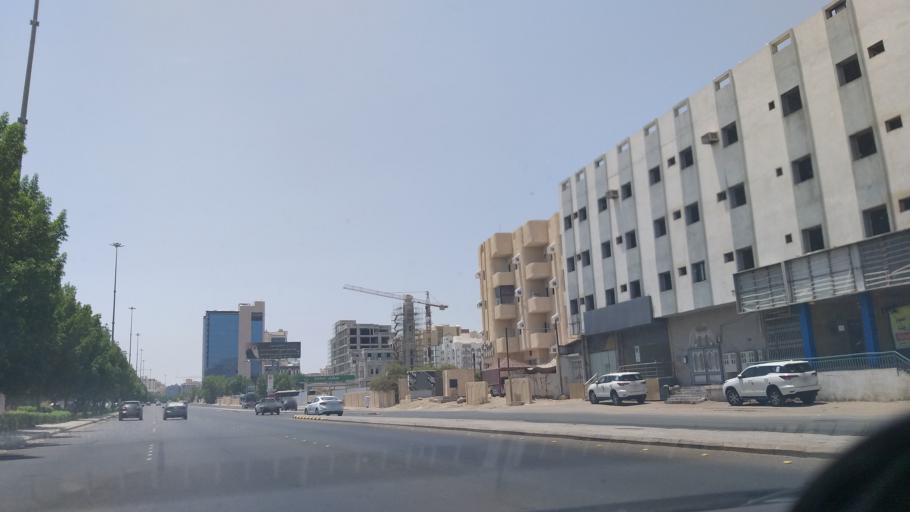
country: SA
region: Makkah
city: Mecca
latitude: 21.3958
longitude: 39.8047
